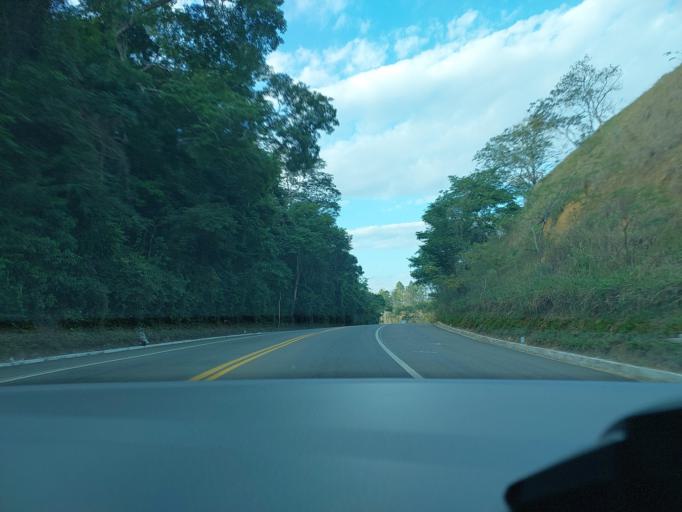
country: BR
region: Minas Gerais
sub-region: Muriae
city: Muriae
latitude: -21.1284
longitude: -42.2896
